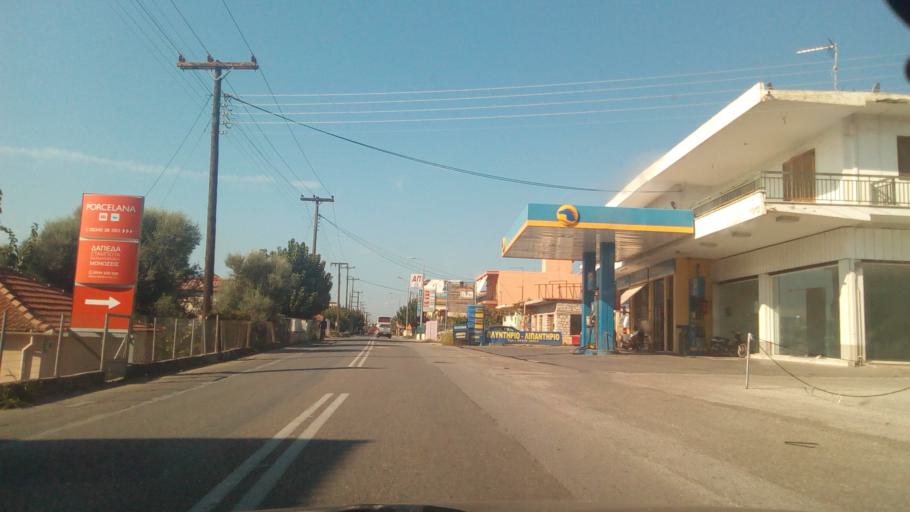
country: GR
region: West Greece
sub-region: Nomos Aitolias kai Akarnanias
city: Nafpaktos
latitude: 38.3994
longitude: 21.8502
